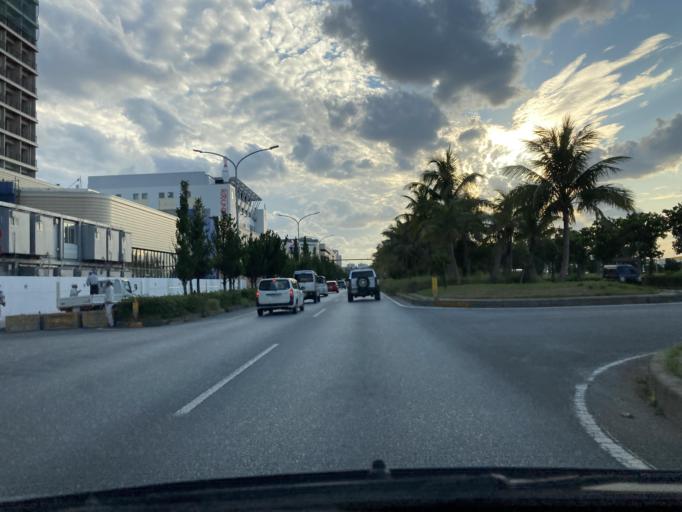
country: JP
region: Okinawa
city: Ginowan
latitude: 26.2776
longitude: 127.7322
